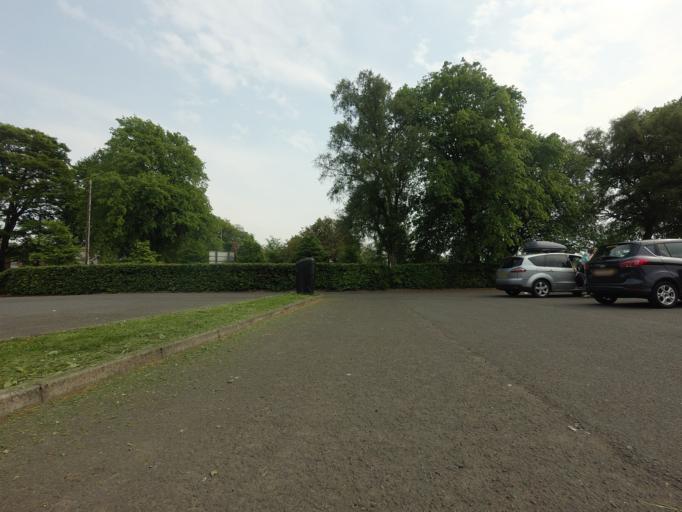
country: GB
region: Scotland
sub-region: Fife
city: Townhill
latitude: 56.0925
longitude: -3.4412
